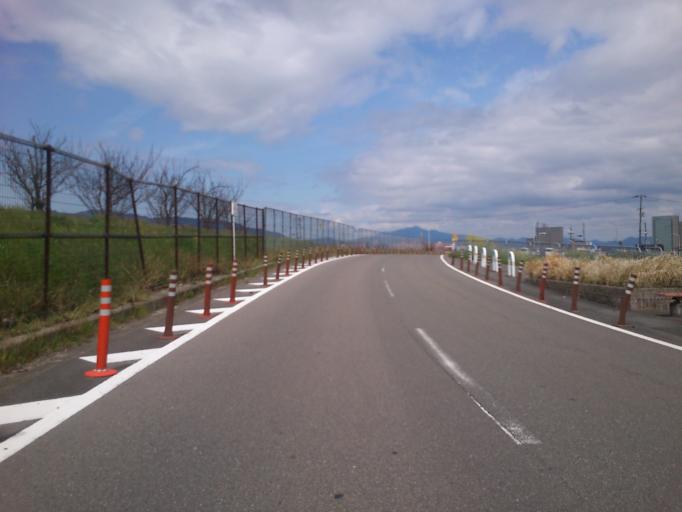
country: JP
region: Kyoto
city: Yawata
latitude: 34.9097
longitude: 135.7021
